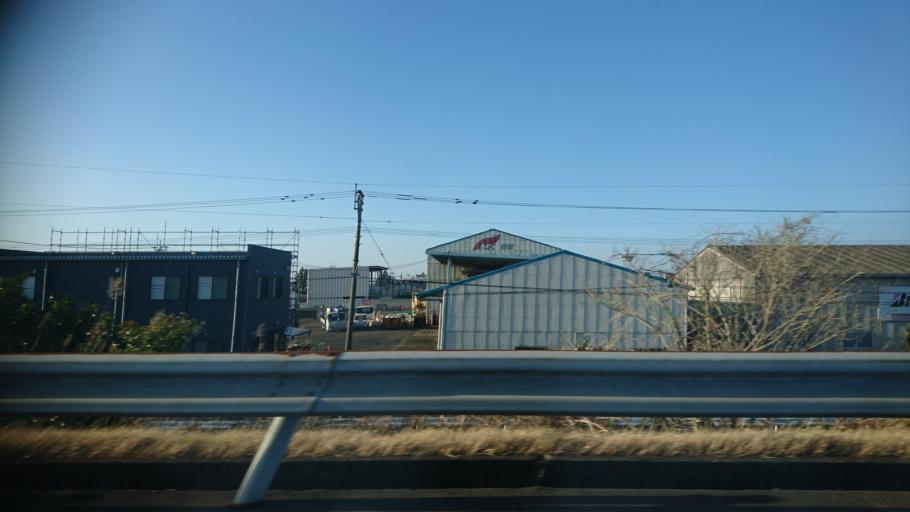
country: JP
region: Miyazaki
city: Miyakonojo
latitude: 31.7844
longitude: 131.1423
